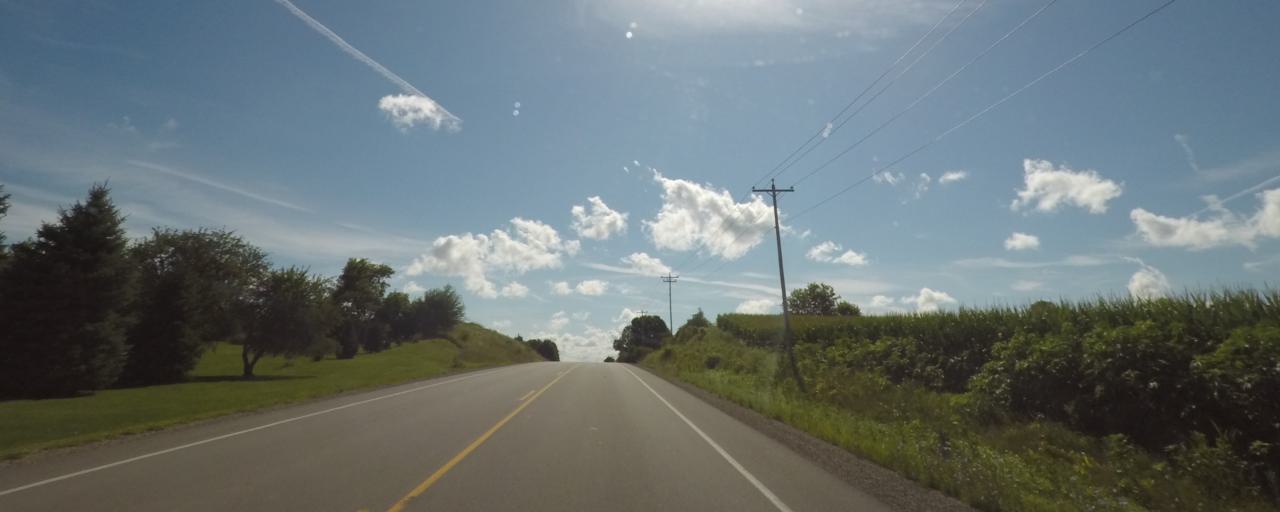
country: US
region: Wisconsin
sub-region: Jefferson County
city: Ixonia
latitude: 43.0678
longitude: -88.6200
